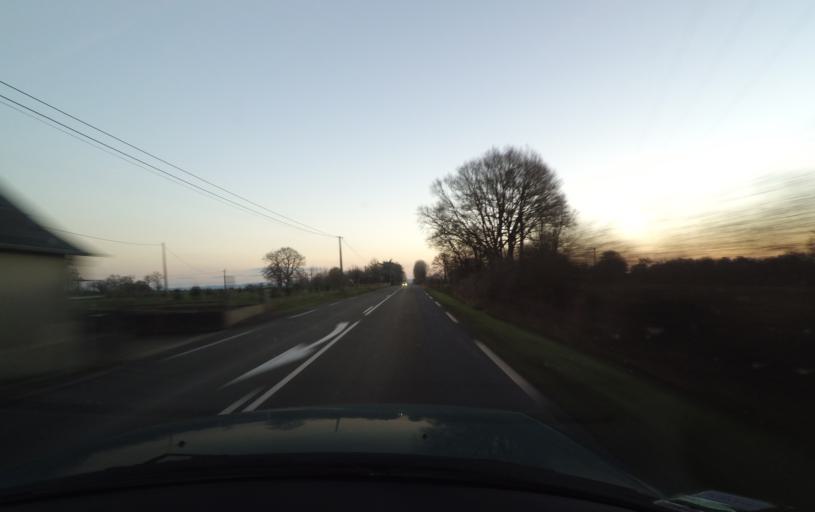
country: FR
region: Pays de la Loire
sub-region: Departement de la Mayenne
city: Vaiges
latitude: 48.1155
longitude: -0.4763
